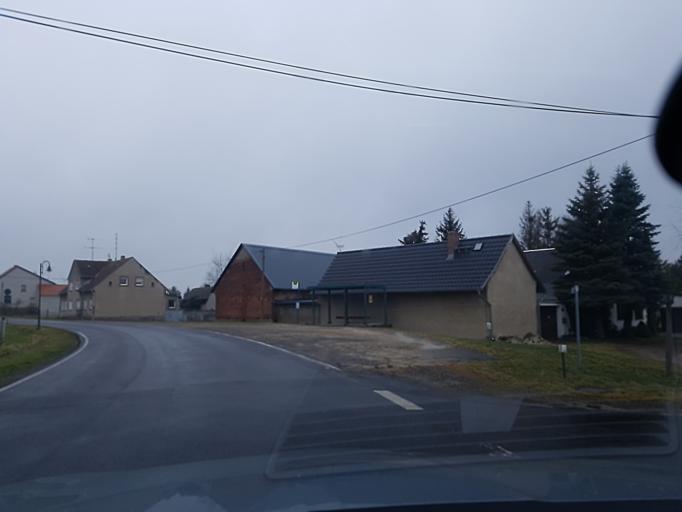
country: DE
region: Brandenburg
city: Schonborn
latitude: 51.6673
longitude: 13.4715
